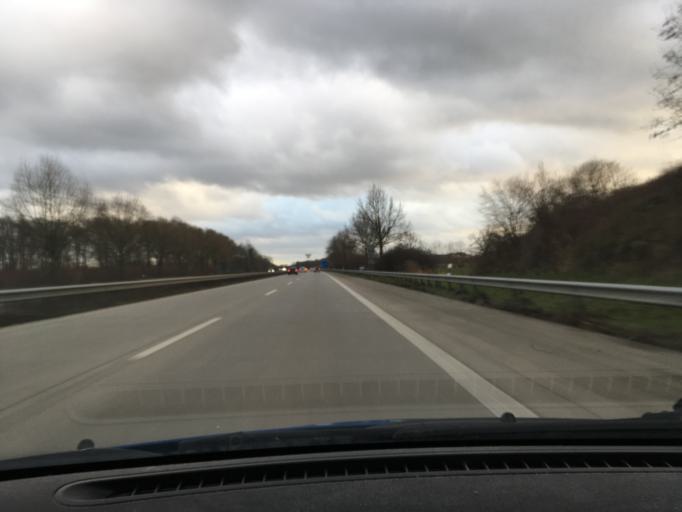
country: DE
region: Schleswig-Holstein
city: Kolln-Reisiek
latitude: 53.7552
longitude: 9.7088
